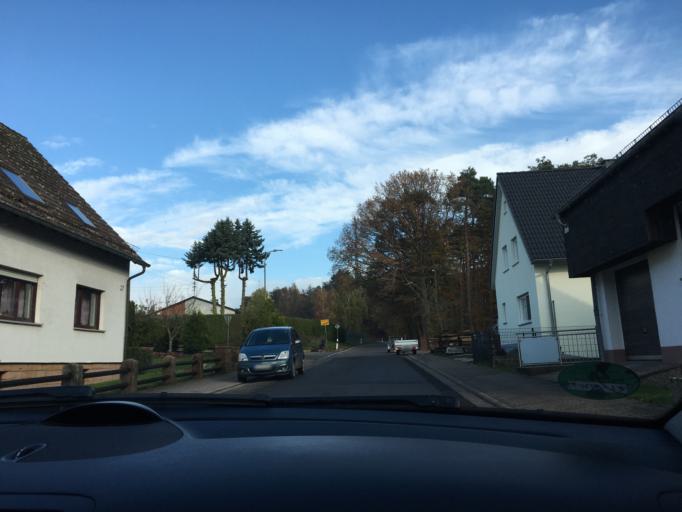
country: DE
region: Rheinland-Pfalz
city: Schopp
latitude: 49.3478
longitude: 7.6884
